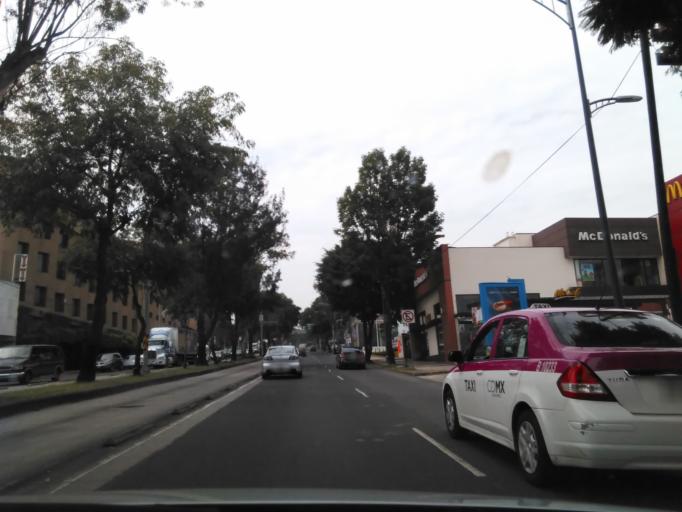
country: MX
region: Mexico City
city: Tlalpan
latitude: 19.2811
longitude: -99.1716
